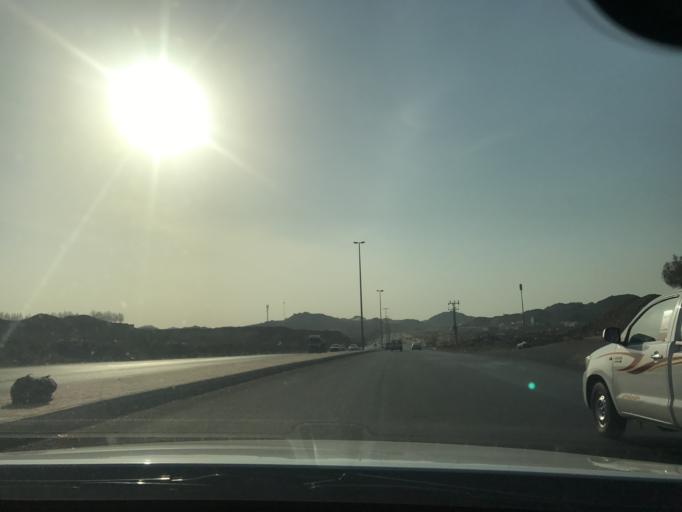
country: SA
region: Makkah
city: Jeddah
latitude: 21.4126
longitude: 39.4194
